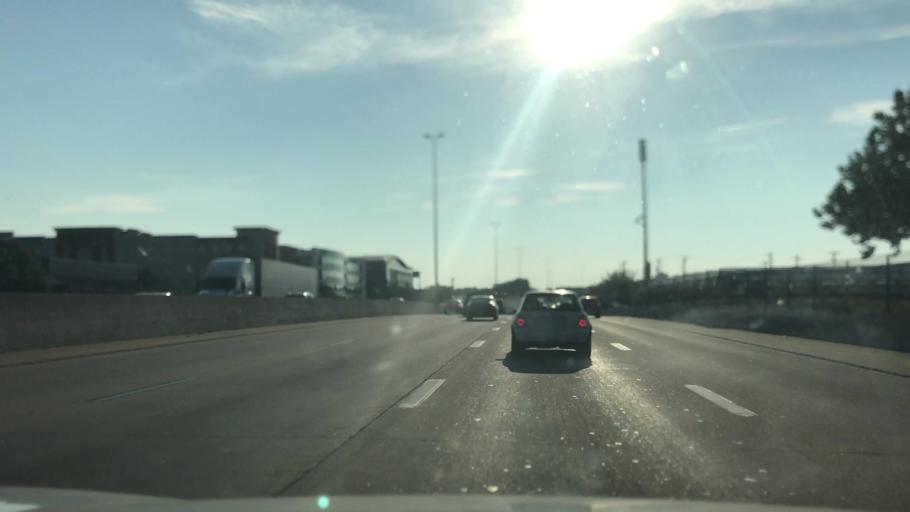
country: US
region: Missouri
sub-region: Saint Louis County
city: University City
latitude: 38.6309
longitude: -90.2789
